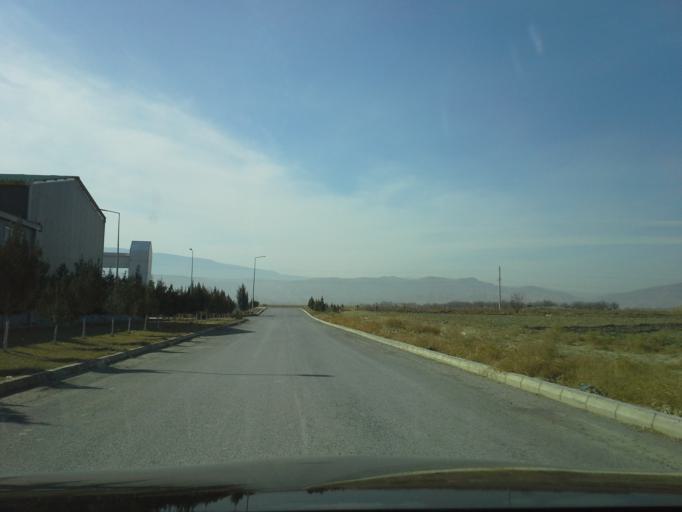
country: TM
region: Ahal
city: Arcabil
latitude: 38.1095
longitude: 57.9693
